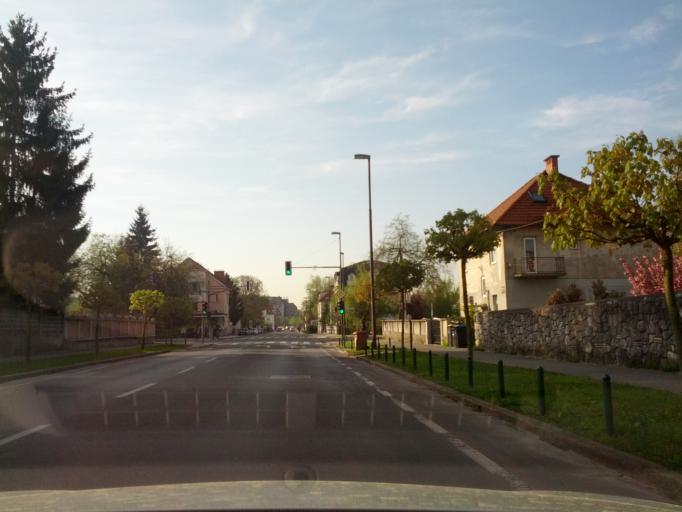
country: SI
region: Ljubljana
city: Ljubljana
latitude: 46.0444
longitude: 14.4971
